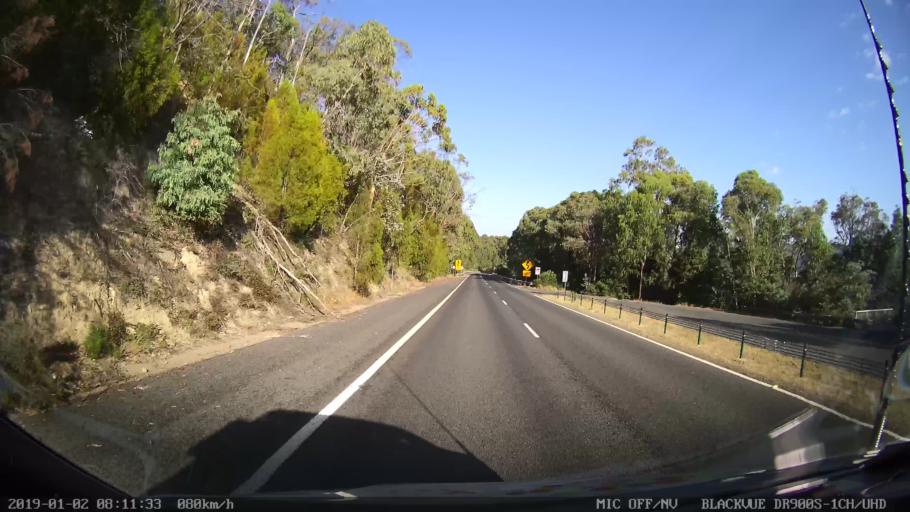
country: AU
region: New South Wales
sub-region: Tumut Shire
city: Tumut
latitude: -35.5951
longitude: 148.3563
